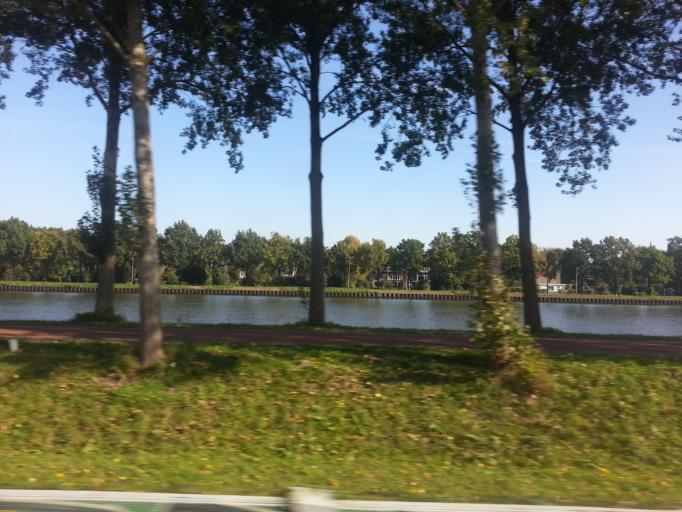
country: NL
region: Utrecht
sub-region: Stichtse Vecht
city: Spechtenkamp
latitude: 52.1384
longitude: 5.0294
